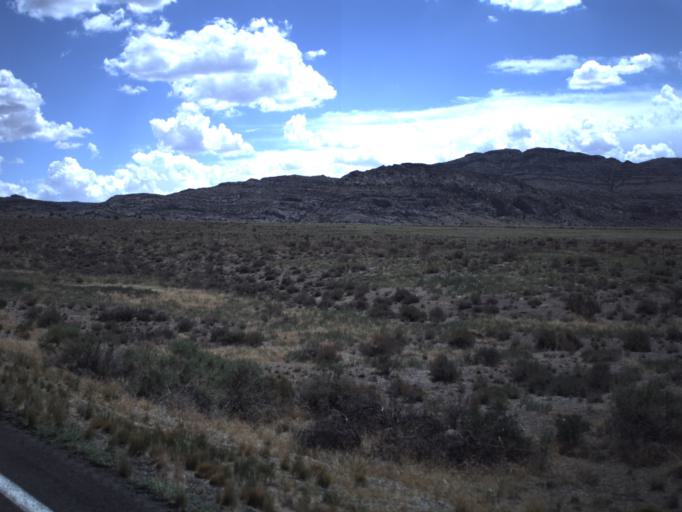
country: US
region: Utah
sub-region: Beaver County
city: Milford
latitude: 39.0751
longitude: -113.6771
